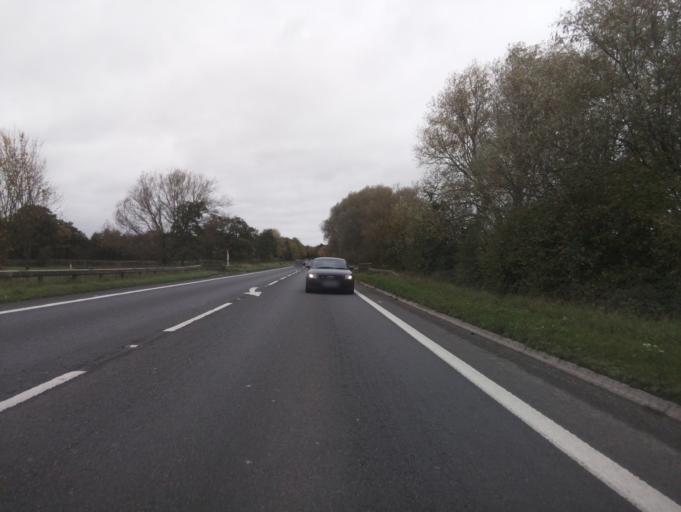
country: GB
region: England
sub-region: Somerset
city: Ilminster
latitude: 50.9435
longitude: -2.9519
